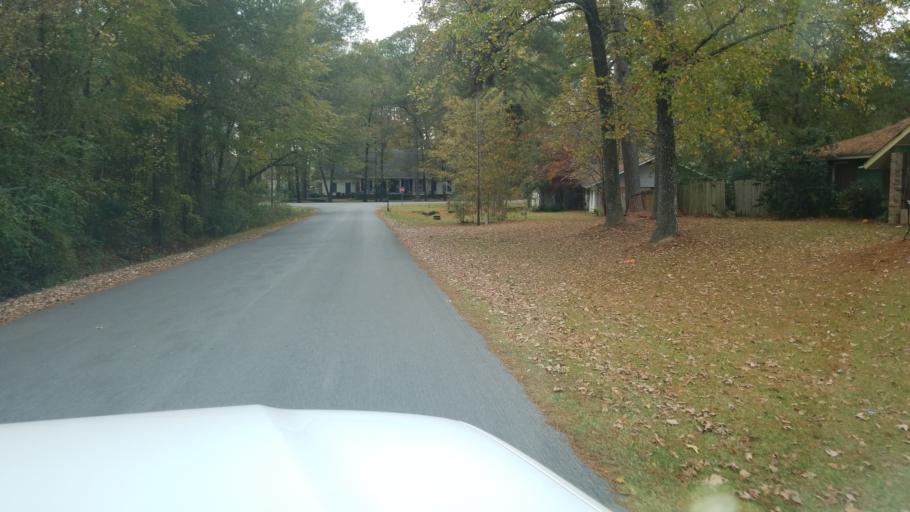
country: US
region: Mississippi
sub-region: Madison County
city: Ridgeland
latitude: 32.3835
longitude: -90.0318
